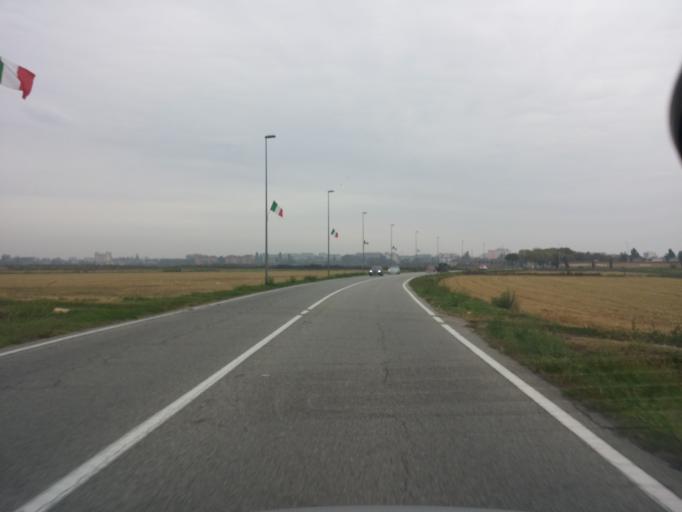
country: IT
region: Piedmont
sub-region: Provincia di Vercelli
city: Vercelli
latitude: 45.3036
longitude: 8.4237
